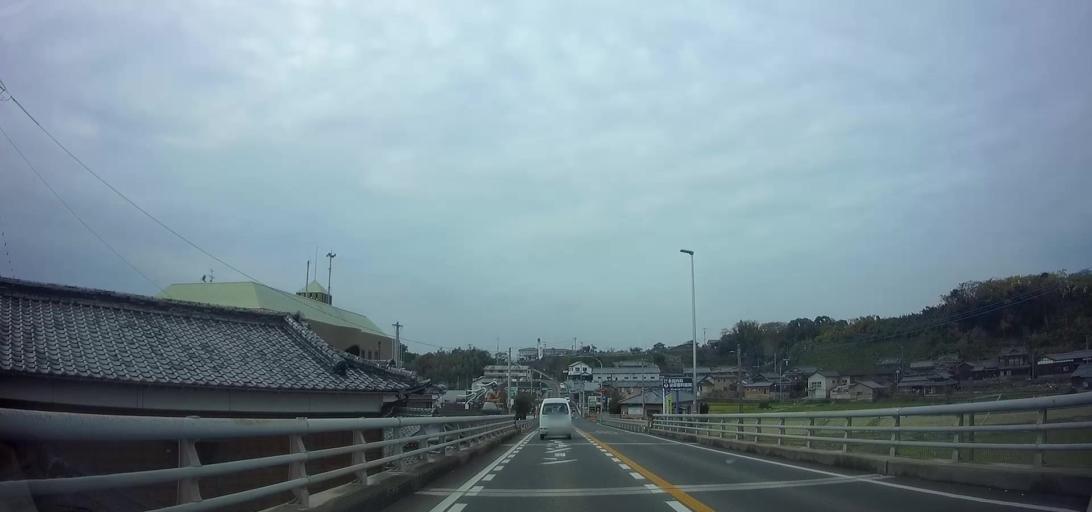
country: JP
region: Nagasaki
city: Shimabara
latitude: 32.6603
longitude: 130.2987
